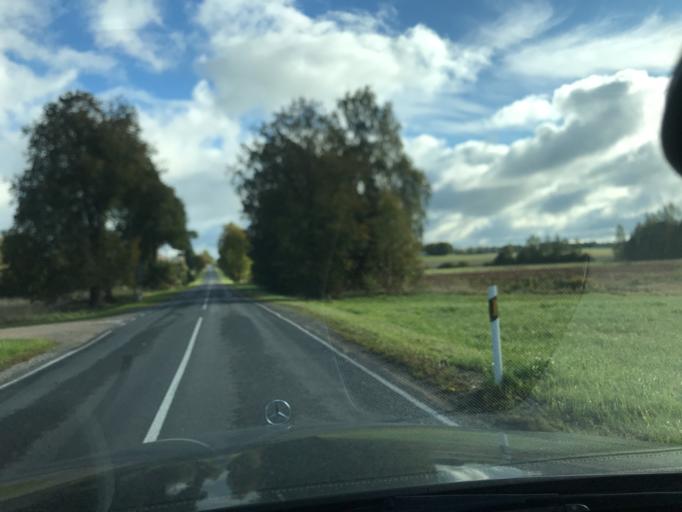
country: EE
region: Tartu
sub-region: Elva linn
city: Elva
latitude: 58.0091
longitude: 26.2305
